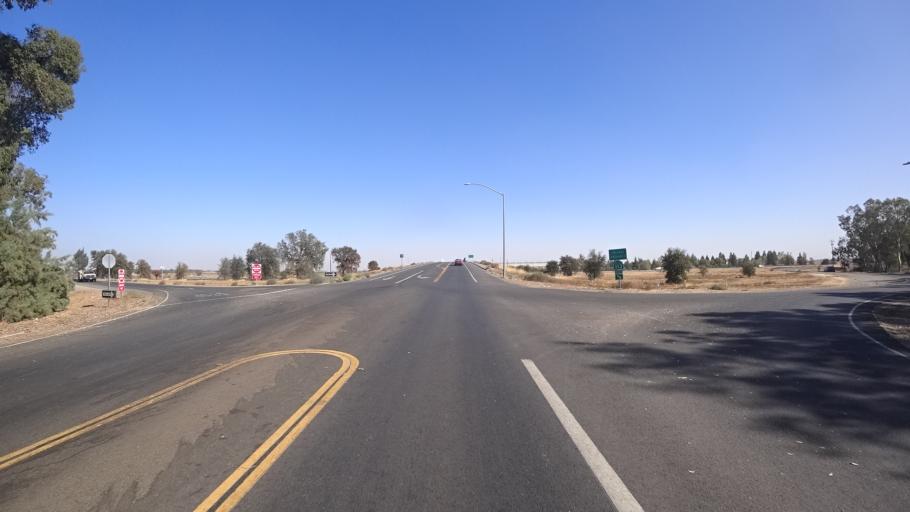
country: US
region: California
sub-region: Yolo County
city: Davis
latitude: 38.5902
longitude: -121.7697
